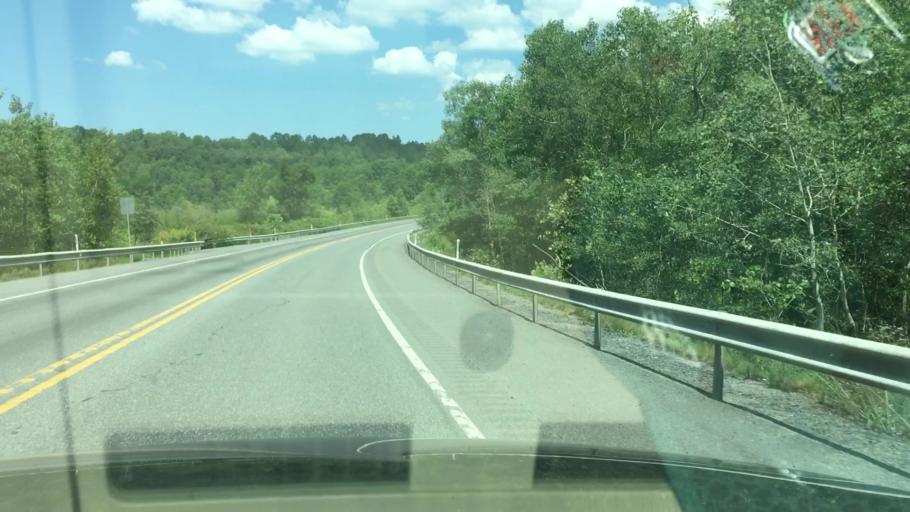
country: US
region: Pennsylvania
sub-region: Northumberland County
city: Kulpmont
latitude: 40.7883
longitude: -76.4464
